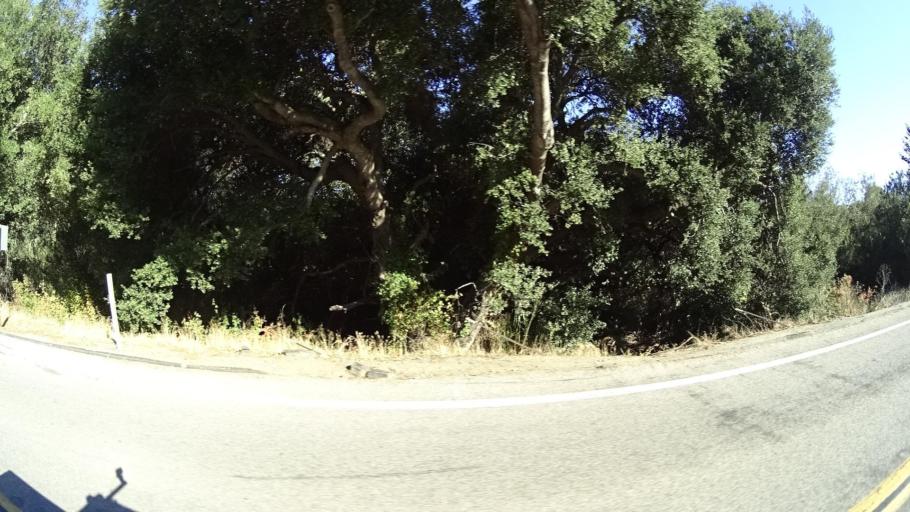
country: US
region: California
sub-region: San Diego County
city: Jamul
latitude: 32.6508
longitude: -116.8661
